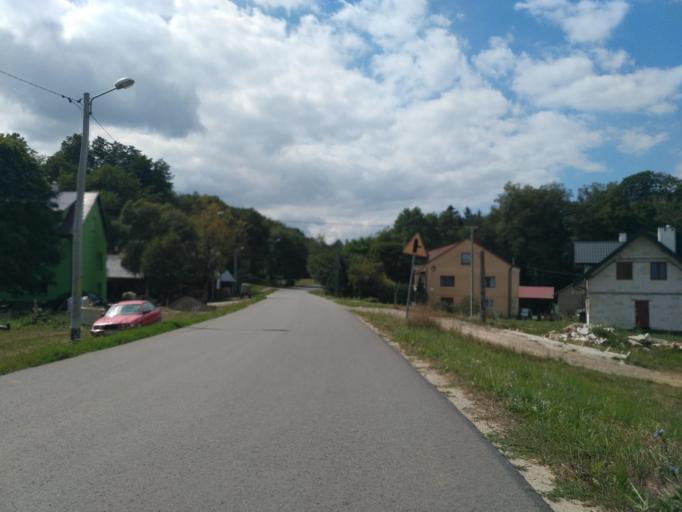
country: PL
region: Subcarpathian Voivodeship
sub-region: Powiat rzeszowski
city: Dynow
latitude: 49.8151
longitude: 22.2743
